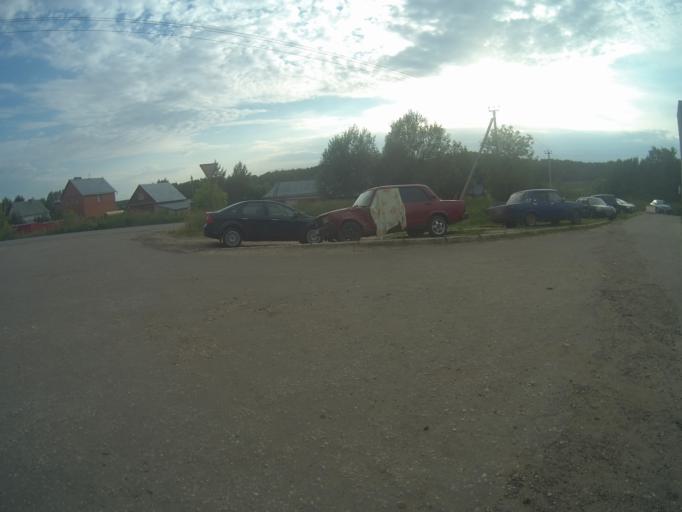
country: RU
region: Vladimir
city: Vladimir
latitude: 56.2228
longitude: 40.4051
